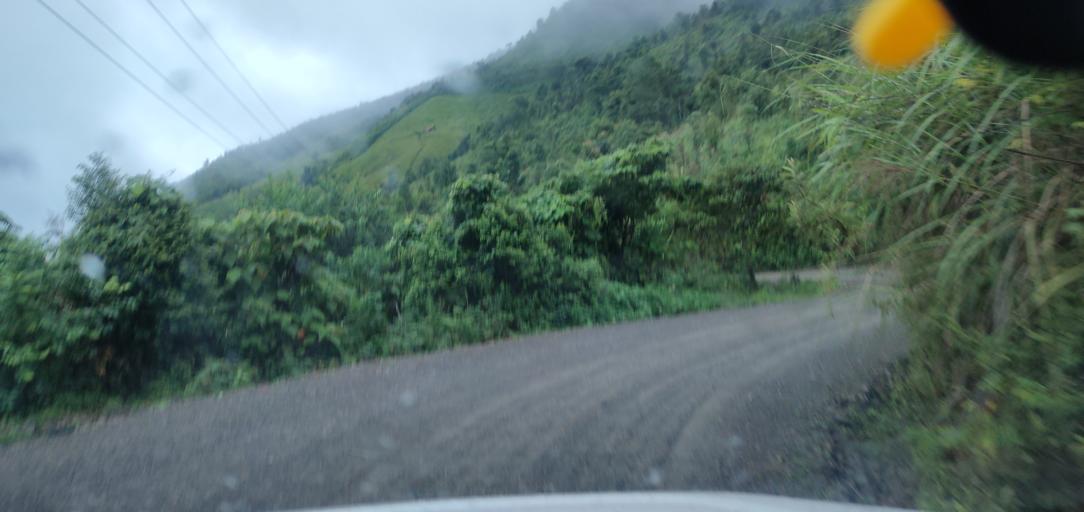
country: LA
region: Phongsali
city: Phongsali
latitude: 21.3964
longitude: 102.2091
